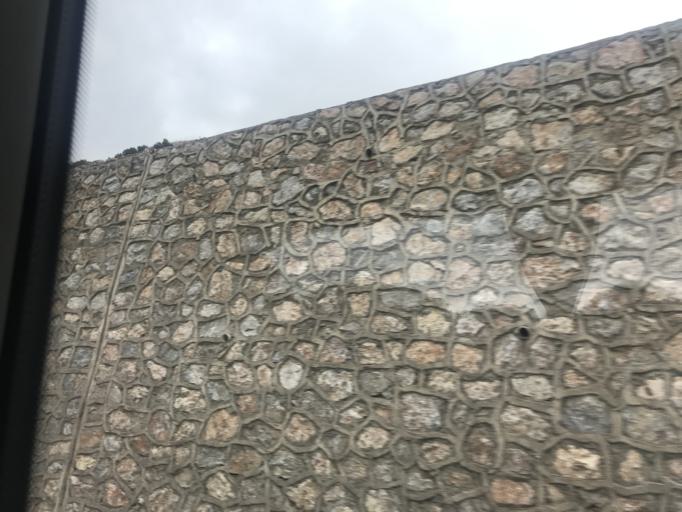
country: TR
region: Balikesir
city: Ivrindi
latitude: 39.6138
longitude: 27.5461
